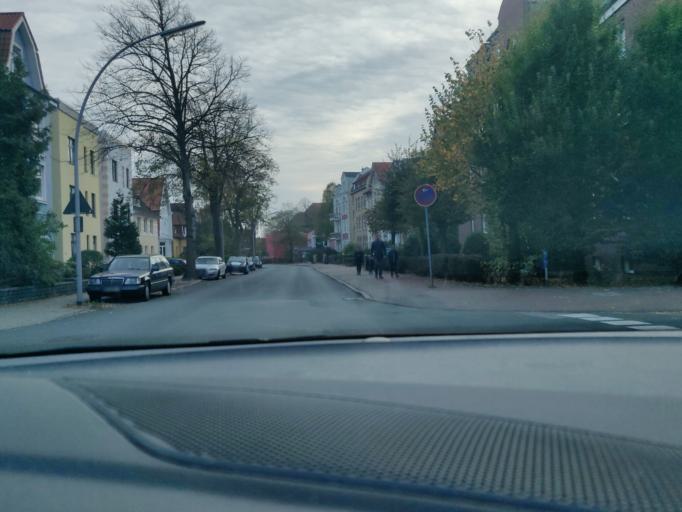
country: DE
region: Lower Saxony
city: Cuxhaven
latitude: 53.8701
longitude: 8.6978
